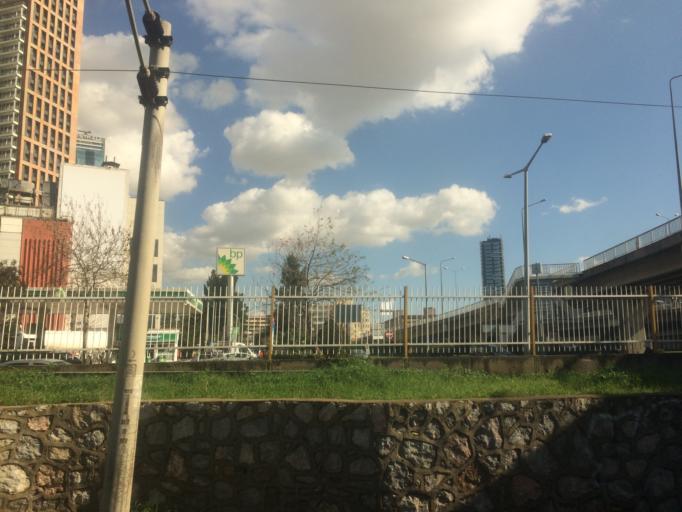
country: TR
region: Izmir
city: Izmir
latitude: 38.4463
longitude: 27.1733
